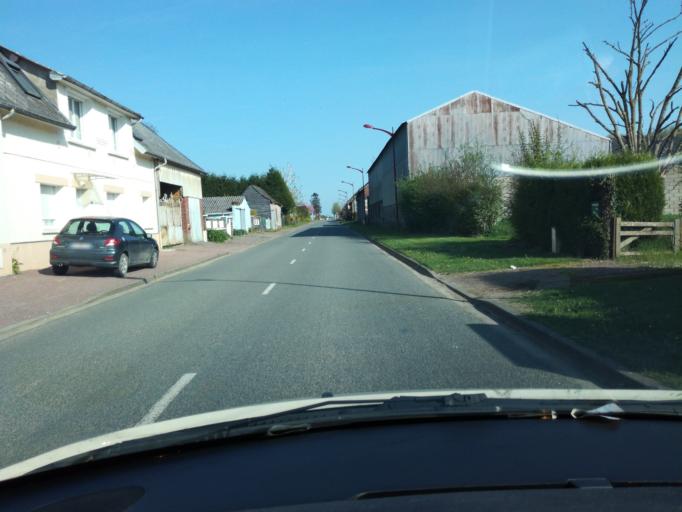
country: FR
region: Picardie
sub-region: Departement de la Somme
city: Hornoy-le-Bourg
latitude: 49.8272
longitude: 1.9378
